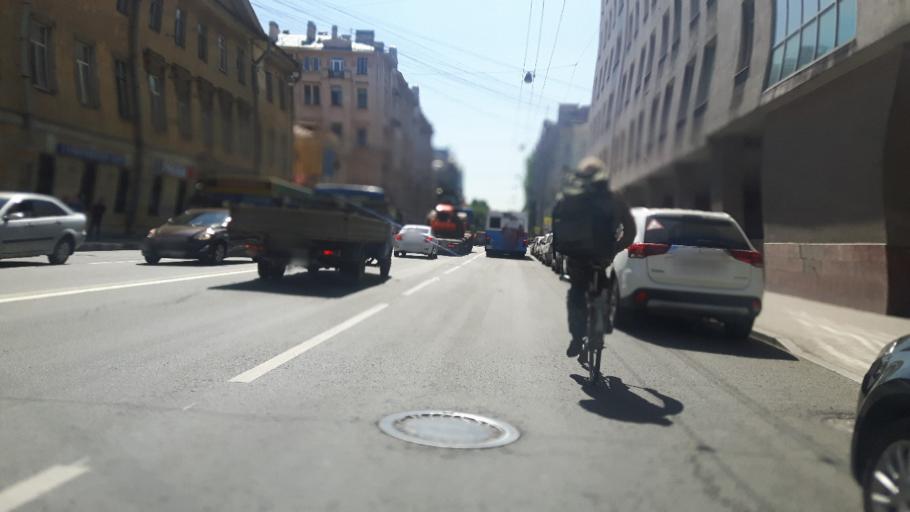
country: RU
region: St.-Petersburg
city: Admiralteisky
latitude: 59.9137
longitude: 30.2974
